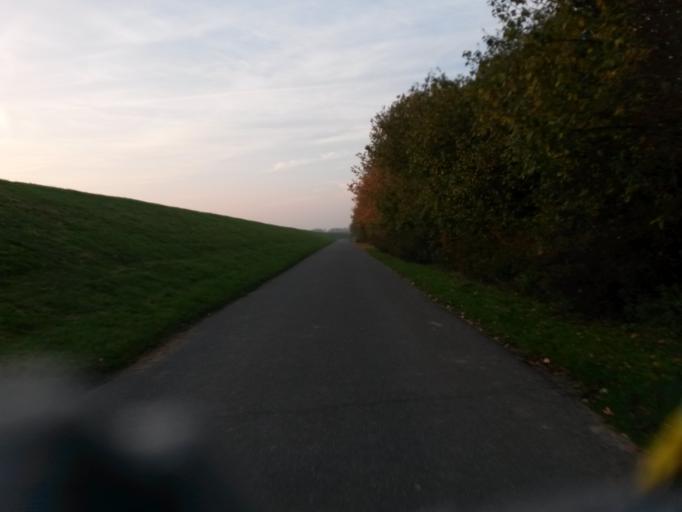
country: DE
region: Bremen
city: Bremen
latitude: 53.0310
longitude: 8.8788
